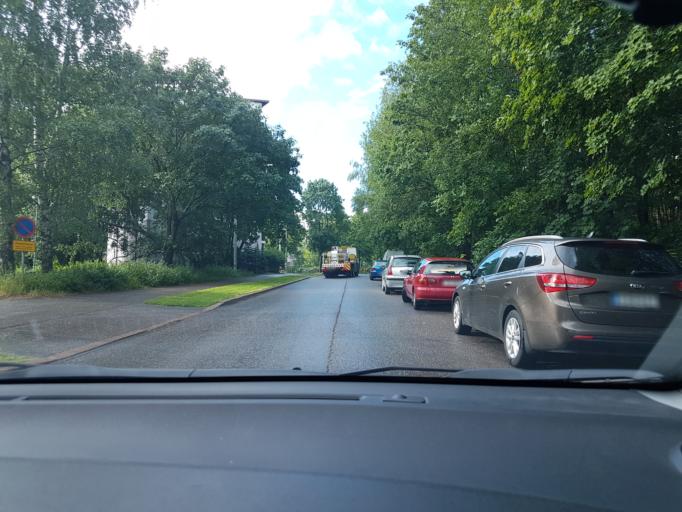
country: FI
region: Uusimaa
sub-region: Helsinki
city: Vantaa
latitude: 60.2379
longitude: 25.0186
